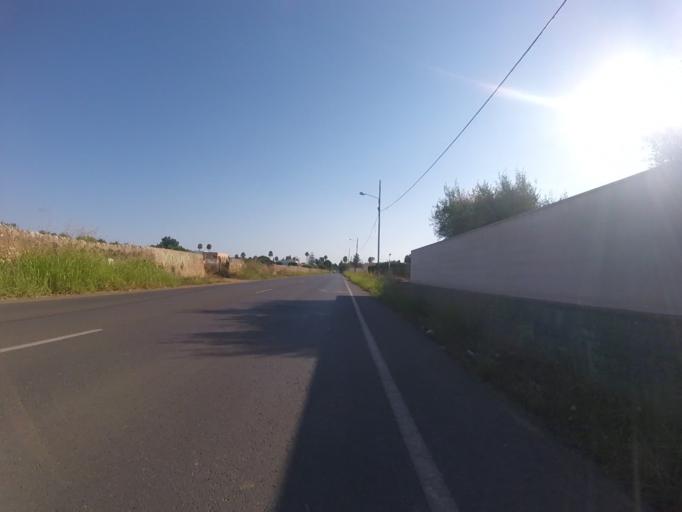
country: ES
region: Valencia
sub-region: Provincia de Castello
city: Benicarlo
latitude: 40.4069
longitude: 0.4173
